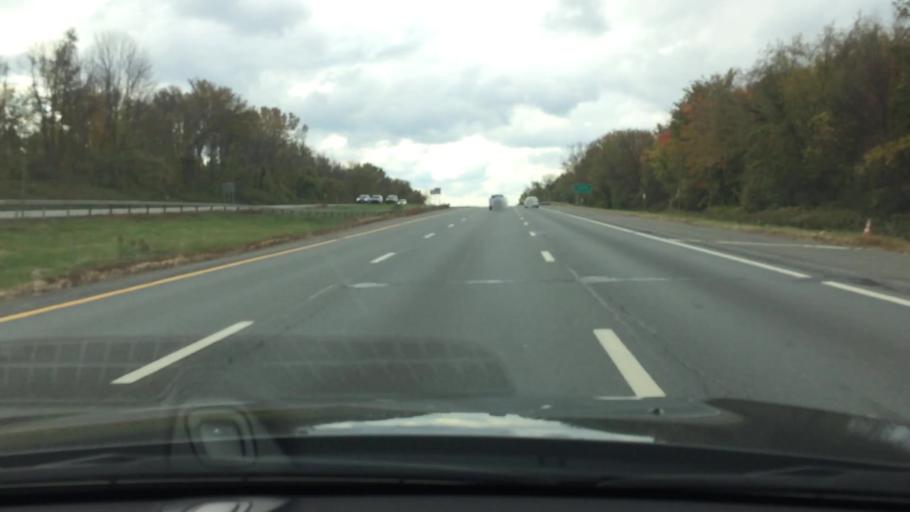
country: US
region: New York
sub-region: Albany County
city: Cohoes
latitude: 42.7831
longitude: -73.7588
